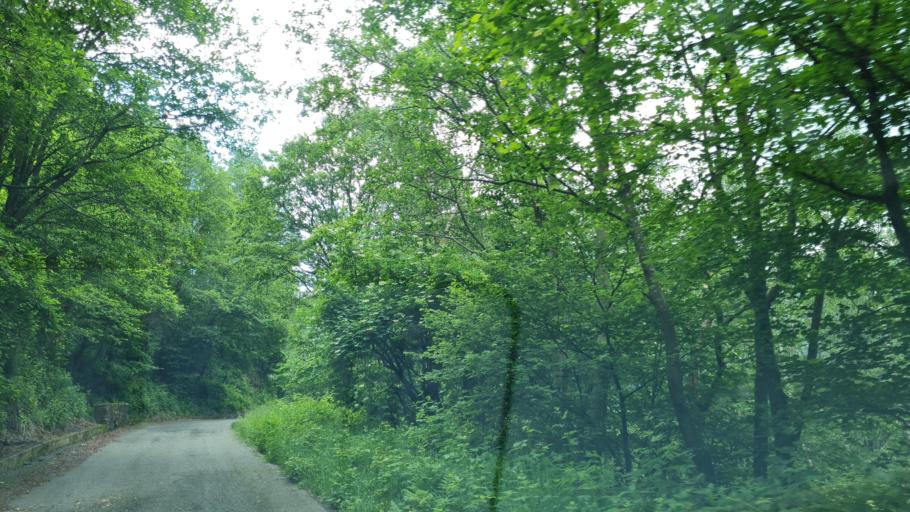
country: IT
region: Piedmont
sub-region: Provincia di Biella
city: Sordevolo
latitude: 45.5985
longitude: 7.9411
